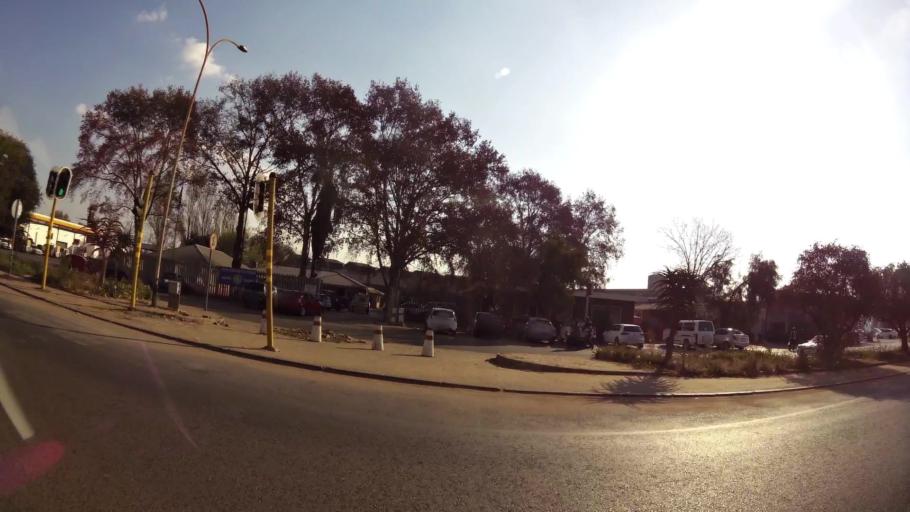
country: ZA
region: Gauteng
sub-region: Ekurhuleni Metropolitan Municipality
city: Tembisa
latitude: -25.9514
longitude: 28.2328
